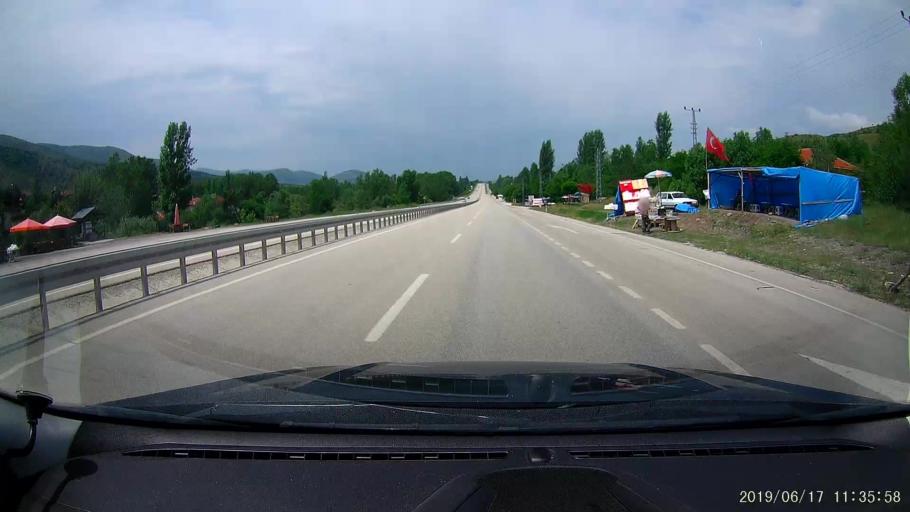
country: TR
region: Cankiri
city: Beloren
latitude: 40.8555
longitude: 33.4592
